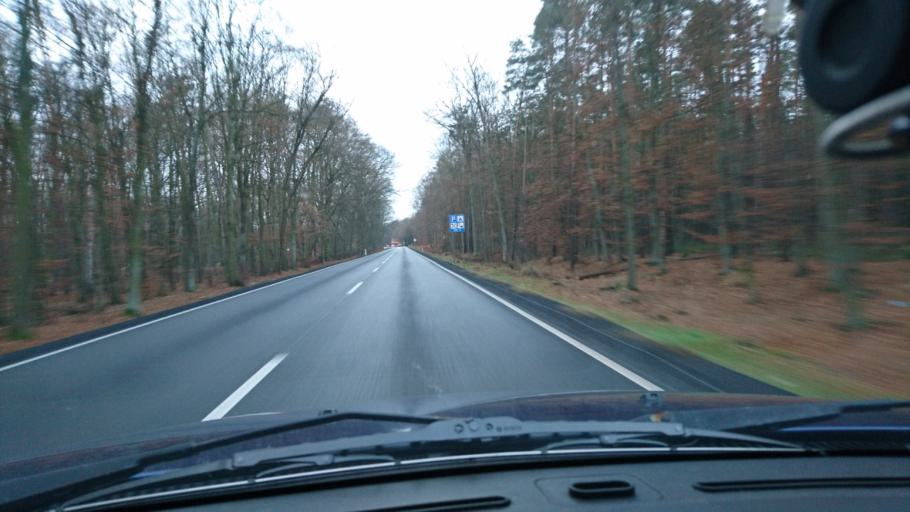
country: PL
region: Opole Voivodeship
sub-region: Powiat kluczborski
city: Kluczbork
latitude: 50.9632
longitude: 18.2839
